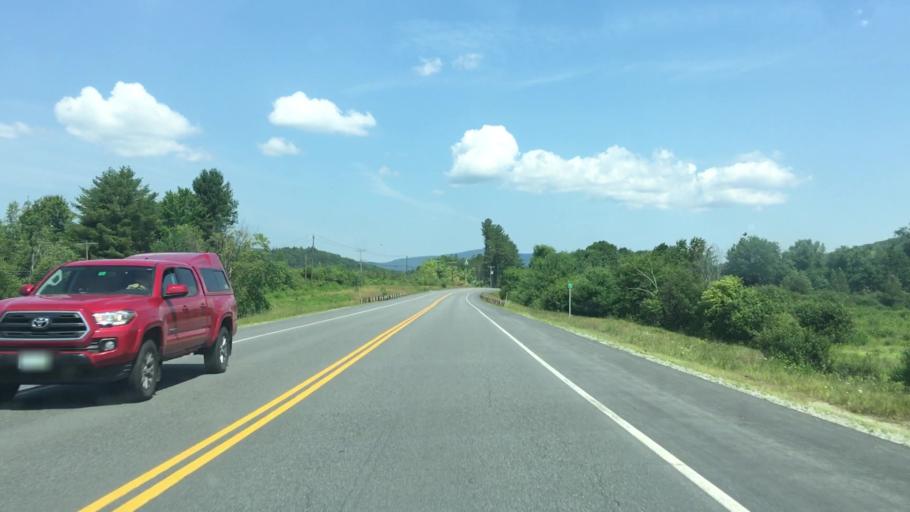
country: US
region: New Hampshire
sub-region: Sullivan County
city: Newport
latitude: 43.3821
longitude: -72.1811
